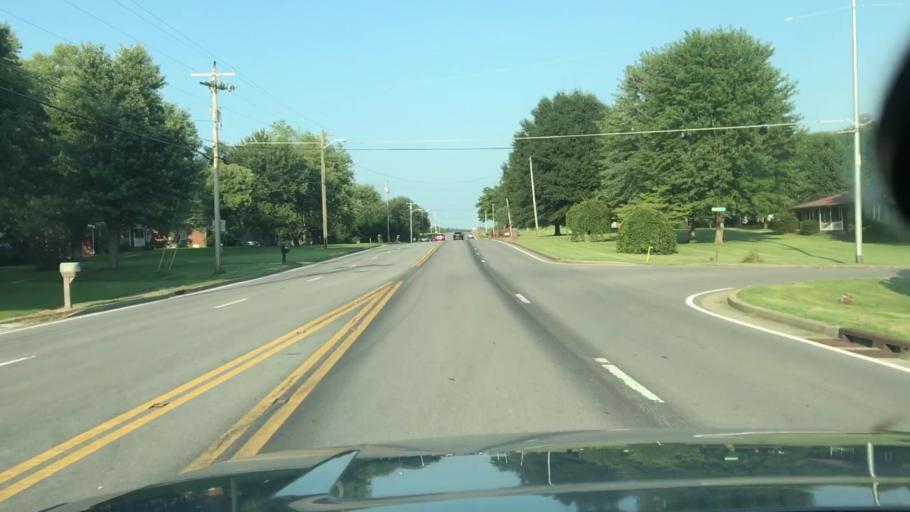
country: US
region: Tennessee
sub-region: Sumner County
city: Portland
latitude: 36.5783
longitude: -86.4775
